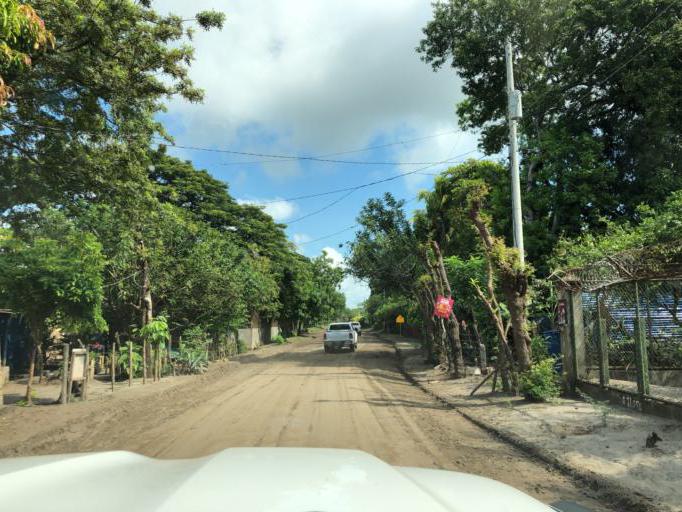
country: NI
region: Granada
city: Granada
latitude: 11.9918
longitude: -85.9381
